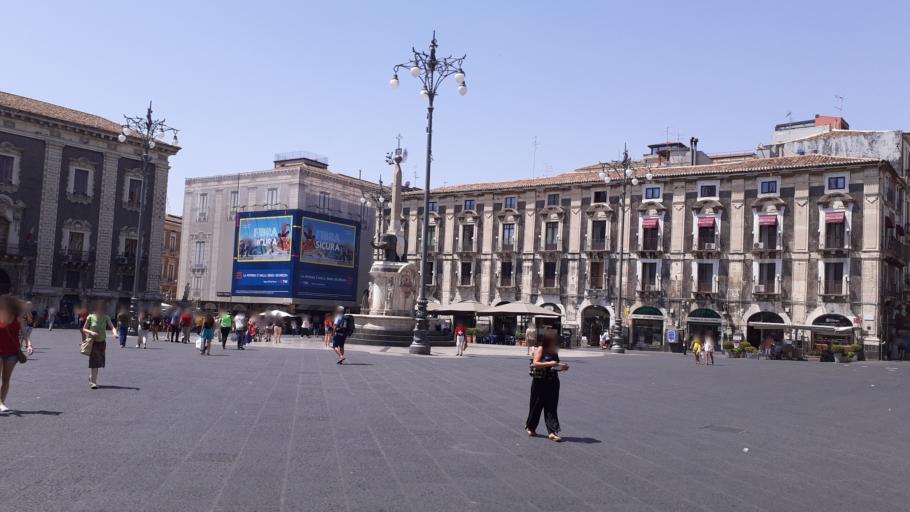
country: IT
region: Sicily
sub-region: Catania
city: Catania
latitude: 37.5028
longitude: 15.0874
